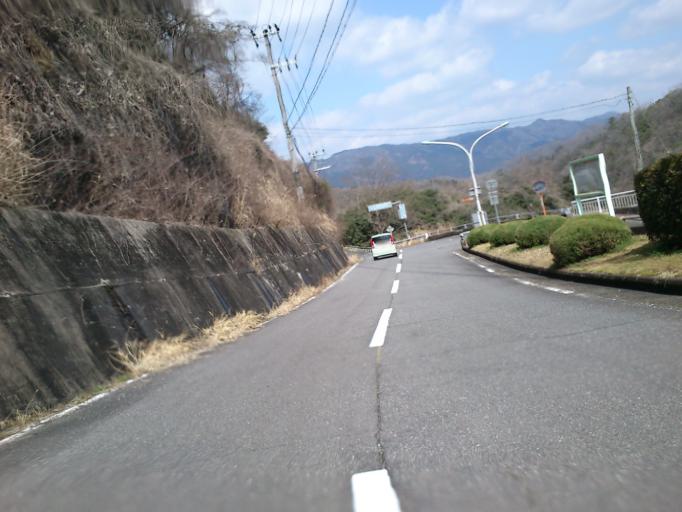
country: JP
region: Mie
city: Ueno-ebisumachi
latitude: 34.7536
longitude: 136.0098
